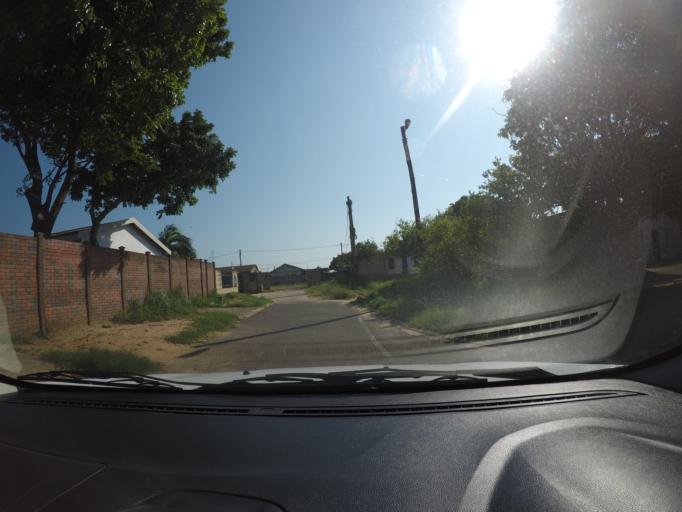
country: ZA
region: KwaZulu-Natal
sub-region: uThungulu District Municipality
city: Richards Bay
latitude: -28.7188
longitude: 32.0417
